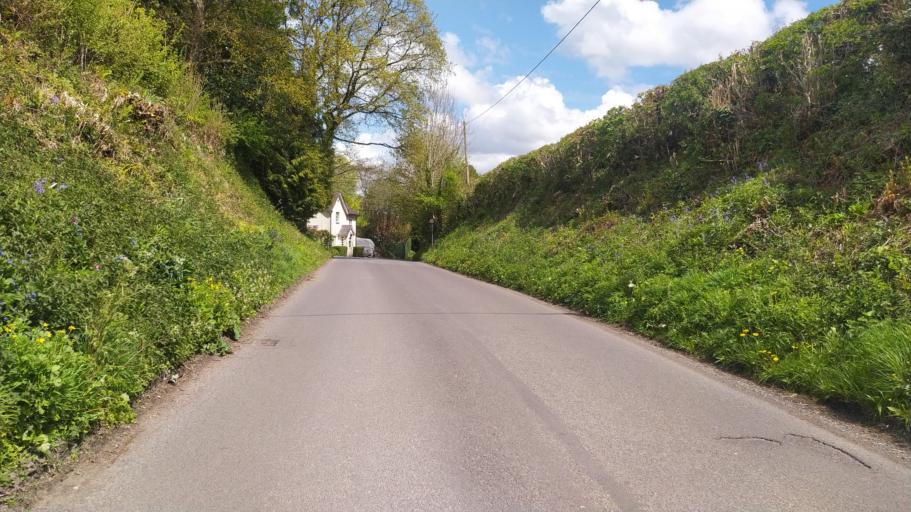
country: GB
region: England
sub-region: Wiltshire
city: Warminster
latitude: 51.1825
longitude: -2.1957
